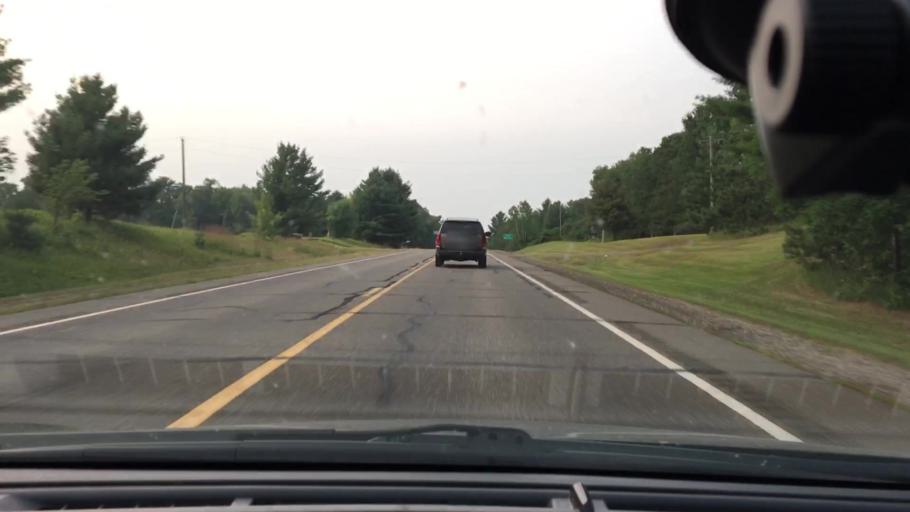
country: US
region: Minnesota
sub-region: Crow Wing County
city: Crosby
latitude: 46.4148
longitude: -93.8727
